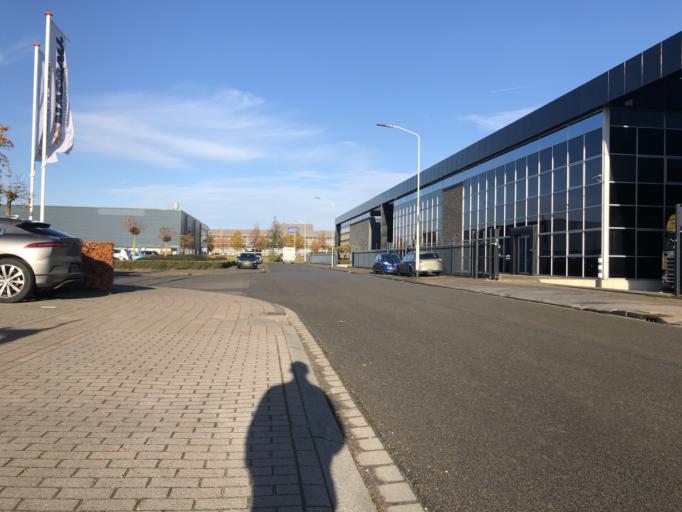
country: NL
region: North Brabant
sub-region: Gemeente Breda
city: Hoge Vucht
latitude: 51.5899
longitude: 4.8409
